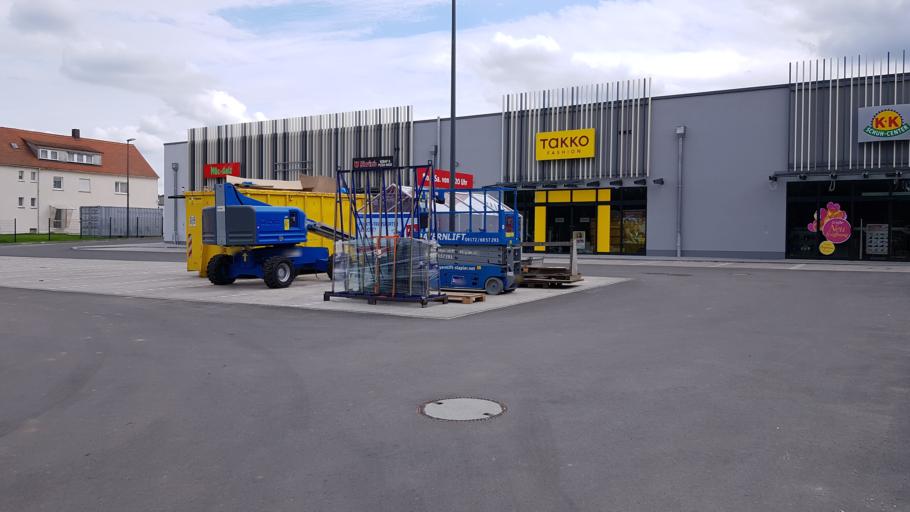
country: DE
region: Bavaria
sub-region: Regierungsbezirk Mittelfranken
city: Hilpoltstein
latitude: 49.1865
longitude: 11.1855
